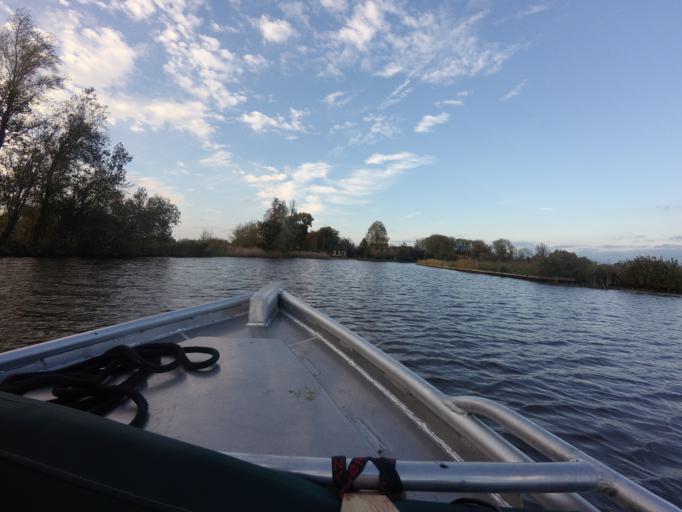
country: NL
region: Overijssel
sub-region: Gemeente Steenwijkerland
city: Blokzijl
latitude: 52.7399
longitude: 5.9934
